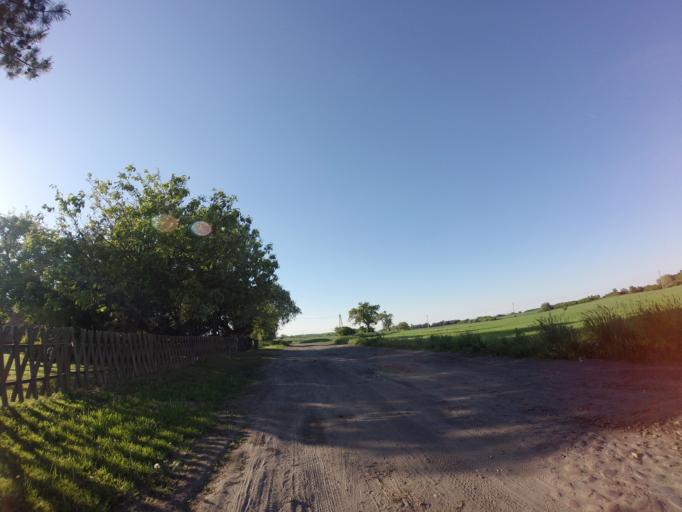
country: PL
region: West Pomeranian Voivodeship
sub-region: Powiat choszczenski
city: Choszczno
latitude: 53.1354
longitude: 15.4393
